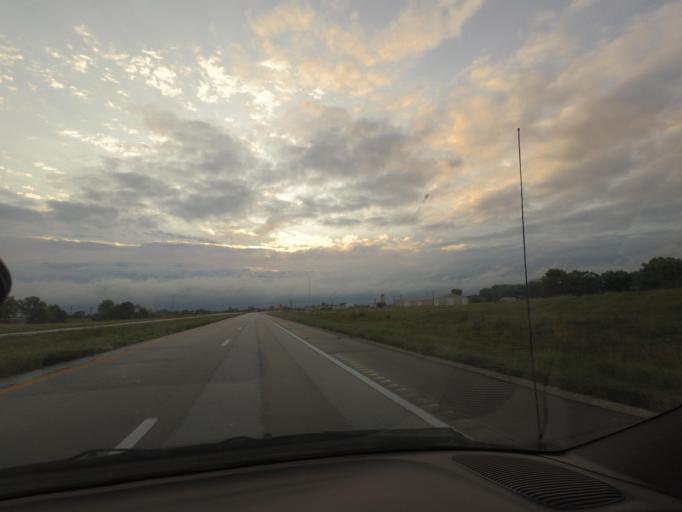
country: US
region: Missouri
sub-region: Shelby County
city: Shelbina
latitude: 39.6978
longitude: -92.0376
